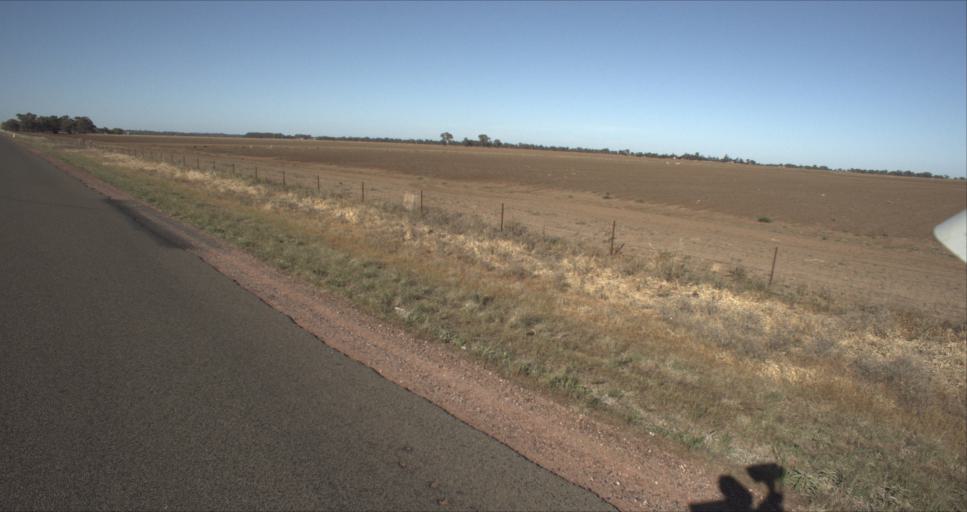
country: AU
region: New South Wales
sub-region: Leeton
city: Leeton
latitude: -34.5706
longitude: 146.2636
